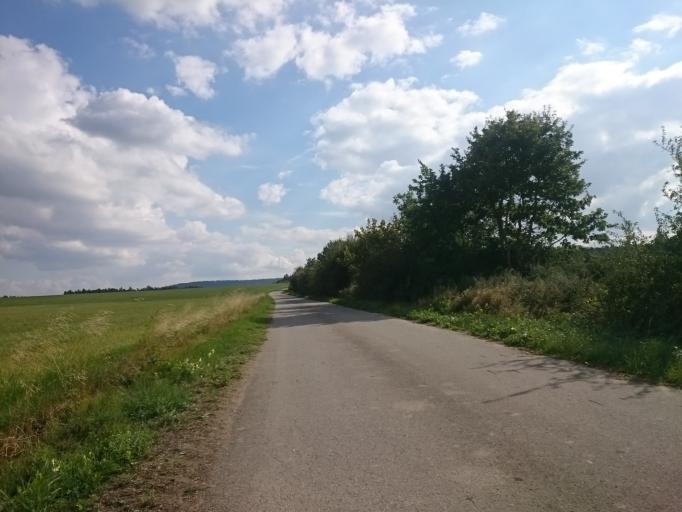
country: DE
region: Bavaria
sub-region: Regierungsbezirk Mittelfranken
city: Heideck
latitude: 49.1265
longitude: 11.1505
